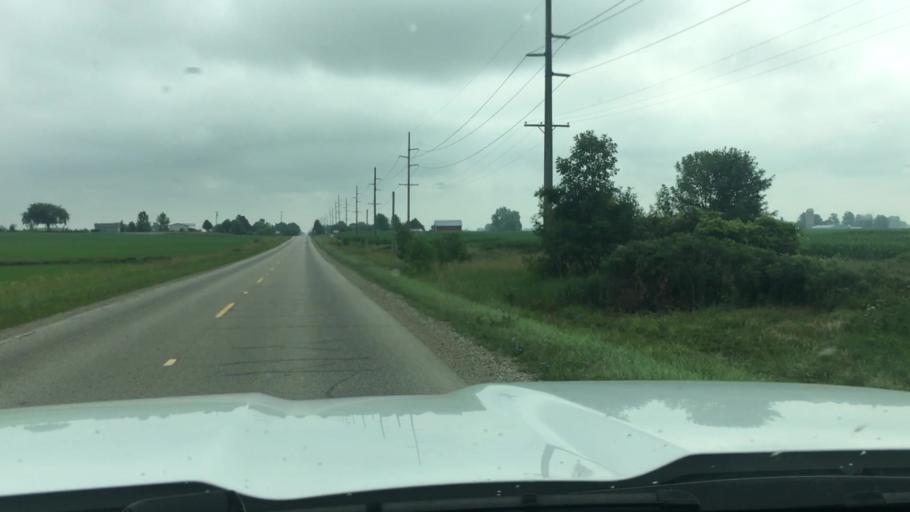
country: US
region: Michigan
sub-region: Sanilac County
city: Brown City
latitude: 43.2561
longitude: -83.0100
